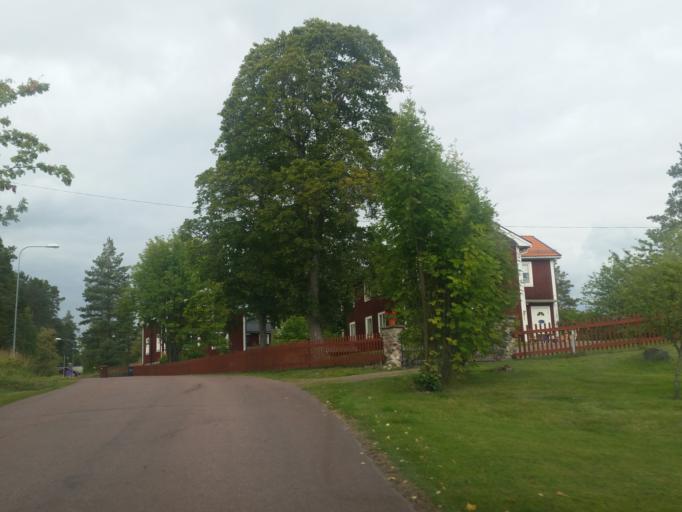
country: SE
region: Dalarna
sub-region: Leksand Municipality
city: Smedby
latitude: 60.6747
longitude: 15.1046
